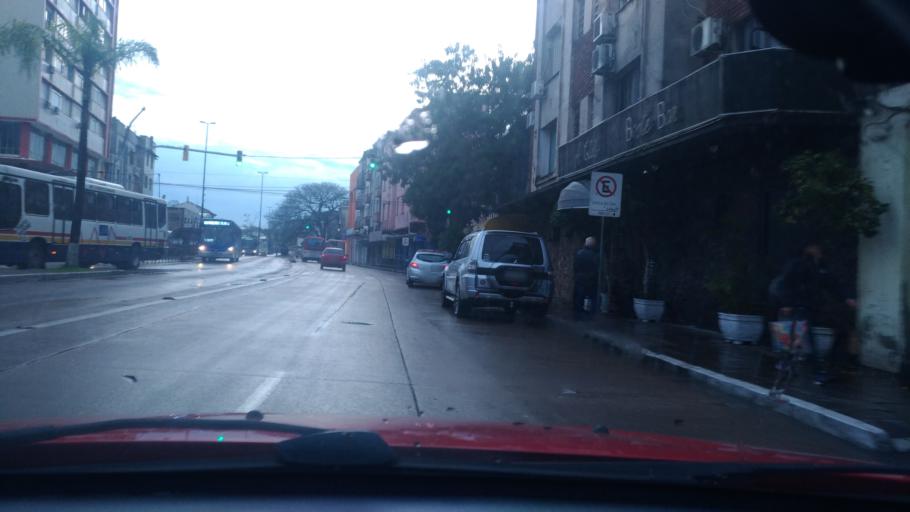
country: BR
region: Rio Grande do Sul
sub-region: Porto Alegre
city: Porto Alegre
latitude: -30.0252
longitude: -51.2152
